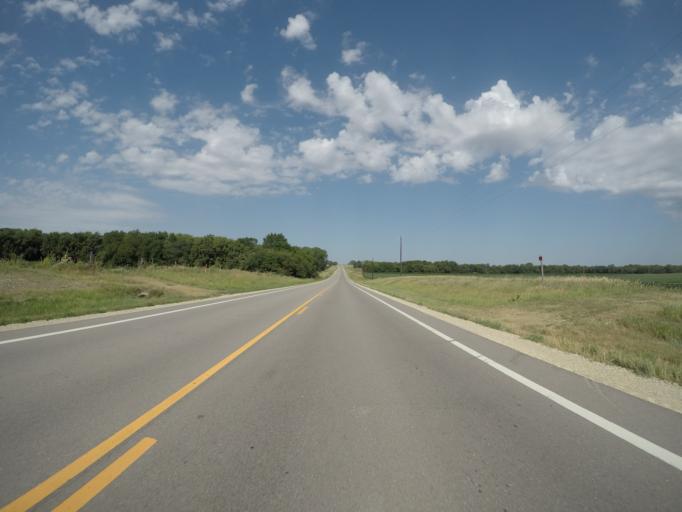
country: US
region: Kansas
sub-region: Clay County
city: Clay Center
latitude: 39.3796
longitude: -97.2299
